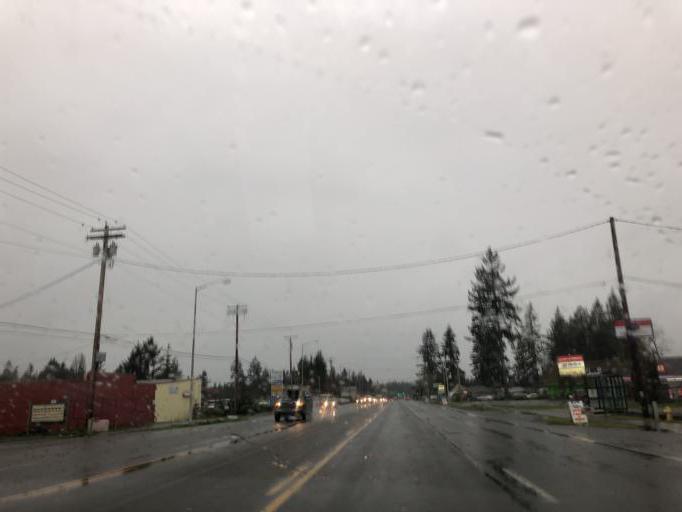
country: US
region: Washington
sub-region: Thurston County
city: Tanglewilde-Thompson Place
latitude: 47.0525
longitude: -122.7862
